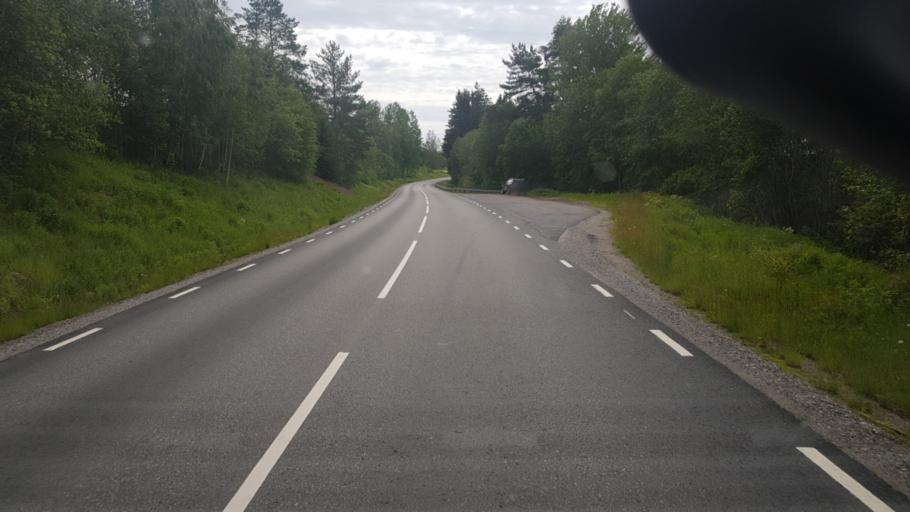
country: SE
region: Vaermland
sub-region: Eda Kommun
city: Amotfors
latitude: 59.8773
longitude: 12.5331
